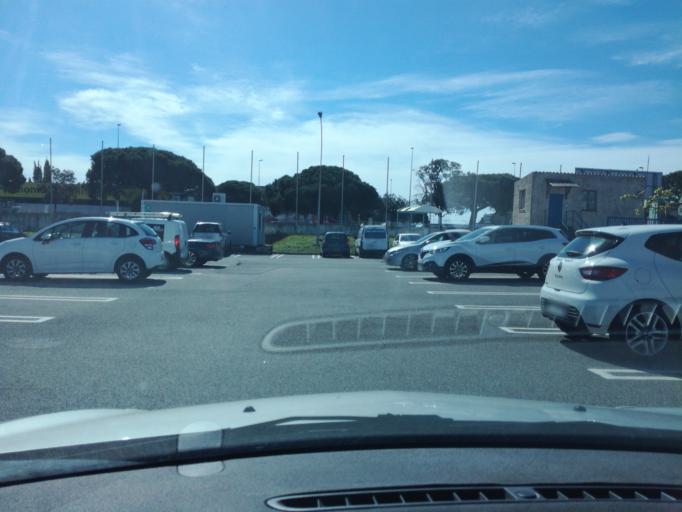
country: FR
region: Provence-Alpes-Cote d'Azur
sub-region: Departement des Alpes-Maritimes
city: Mandelieu-la-Napoule
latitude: 43.5441
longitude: 6.9591
